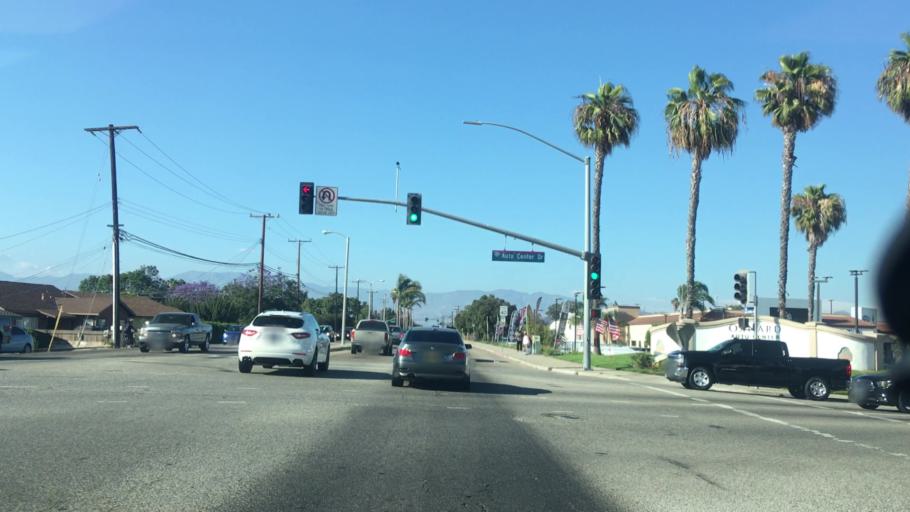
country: US
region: California
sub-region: Ventura County
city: El Rio
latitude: 34.2279
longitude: -119.1580
